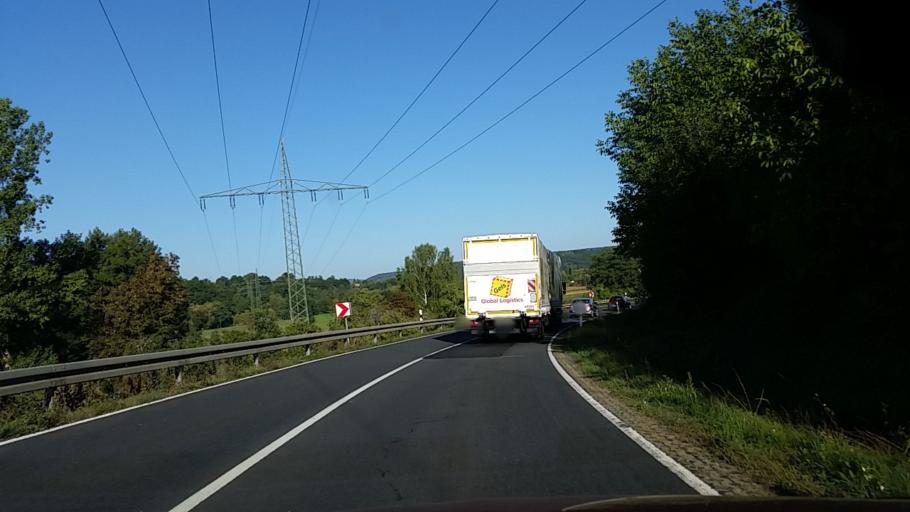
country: DE
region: Bavaria
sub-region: Regierungsbezirk Unterfranken
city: Gossenheim
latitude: 50.0108
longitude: 9.7896
